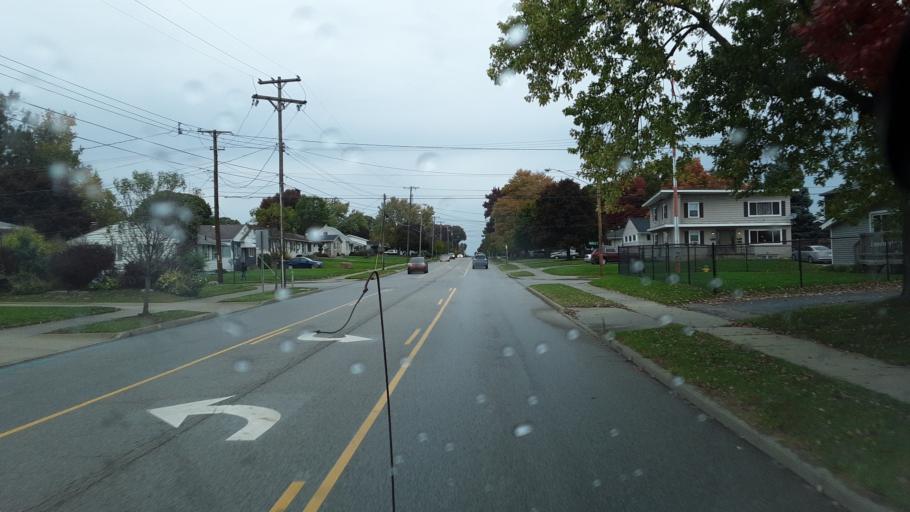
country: US
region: Ohio
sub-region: Summit County
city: Sawyerwood
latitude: 41.0446
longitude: -81.4538
